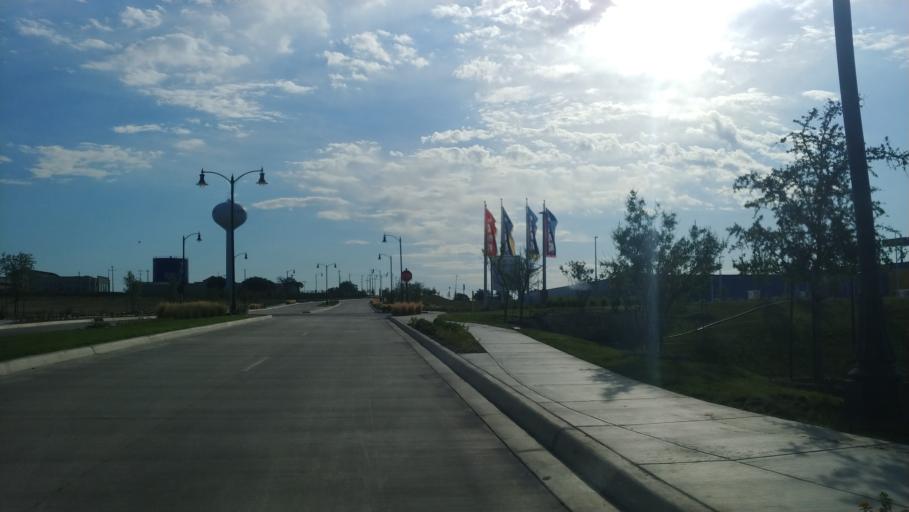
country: US
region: Texas
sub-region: Bexar County
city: Live Oak
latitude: 29.5664
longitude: -98.3415
